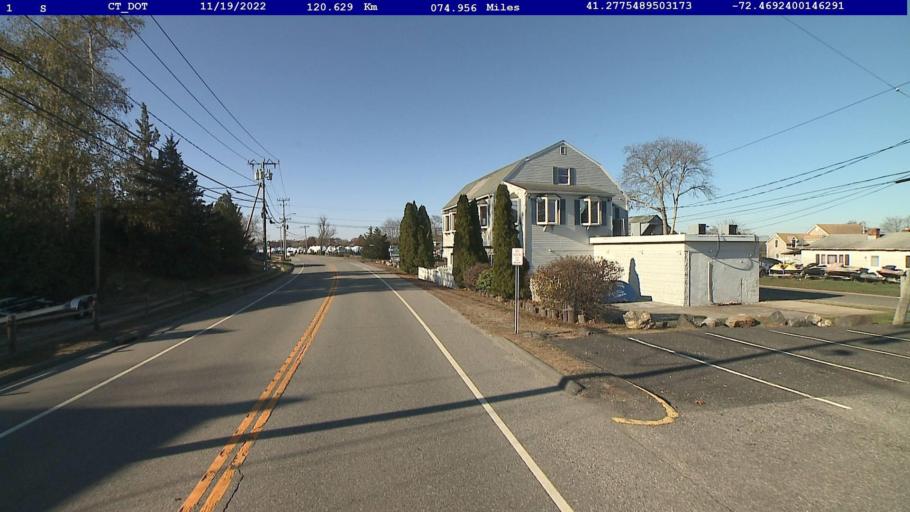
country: US
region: Connecticut
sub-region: Middlesex County
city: Westbrook Center
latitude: 41.2776
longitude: -72.4692
